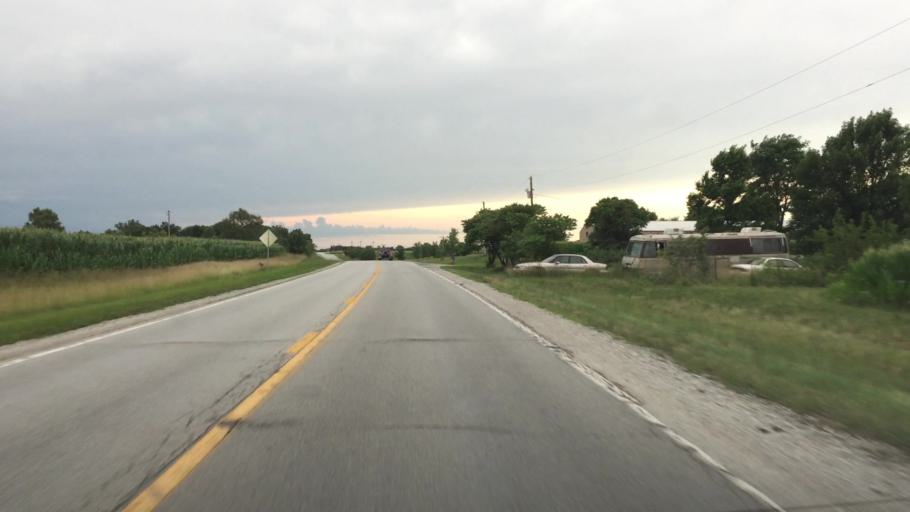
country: US
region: Illinois
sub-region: Hancock County
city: Hamilton
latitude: 40.3771
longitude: -91.3421
